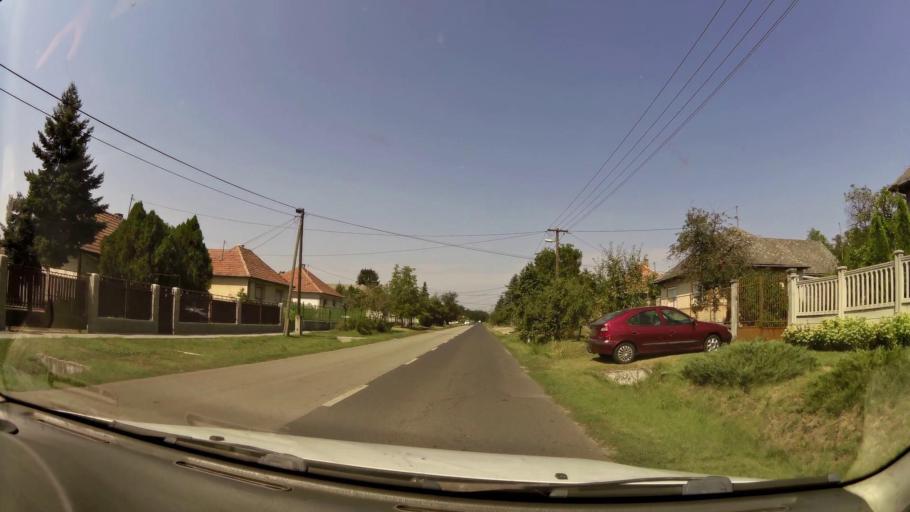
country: HU
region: Pest
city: Tapiosag
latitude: 47.4055
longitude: 19.6207
